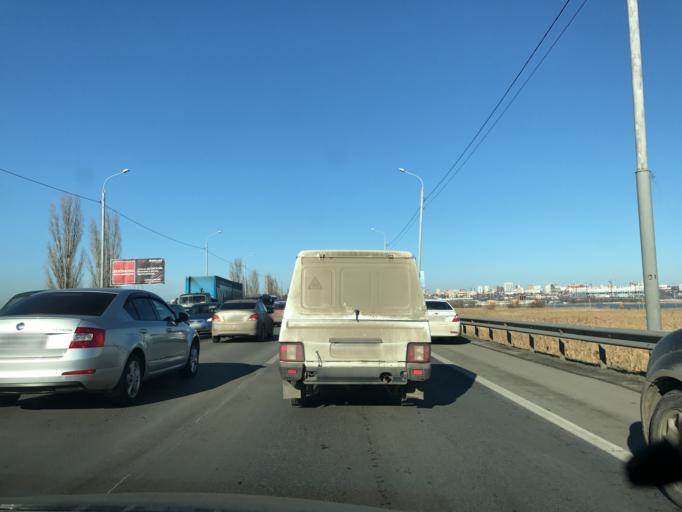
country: RU
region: Rostov
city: Rostov-na-Donu
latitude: 47.1892
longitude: 39.7352
